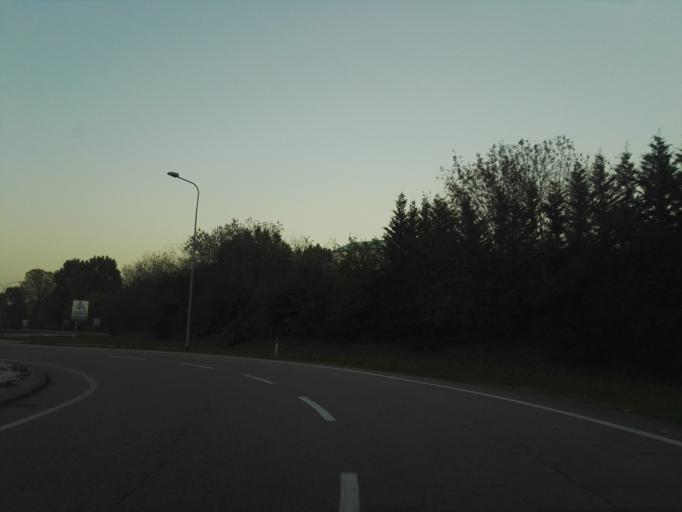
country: IT
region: Lombardy
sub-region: Citta metropolitana di Milano
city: San Bovio-San Felice
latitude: 45.4693
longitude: 9.3037
